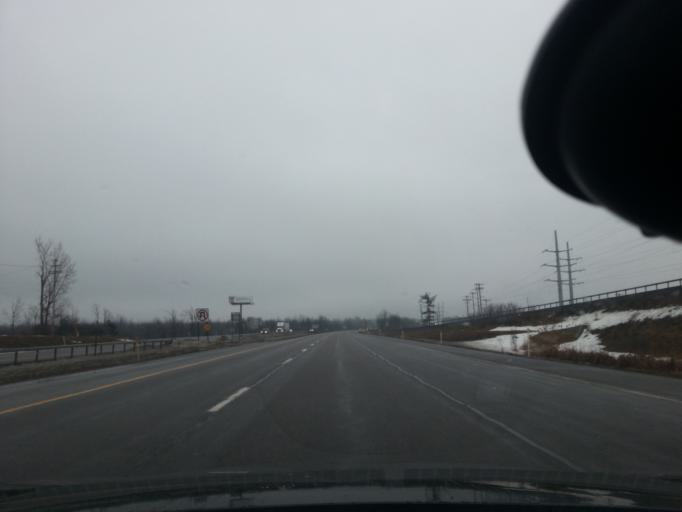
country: US
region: New York
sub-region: Jefferson County
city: Watertown
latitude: 43.9743
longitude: -75.9486
